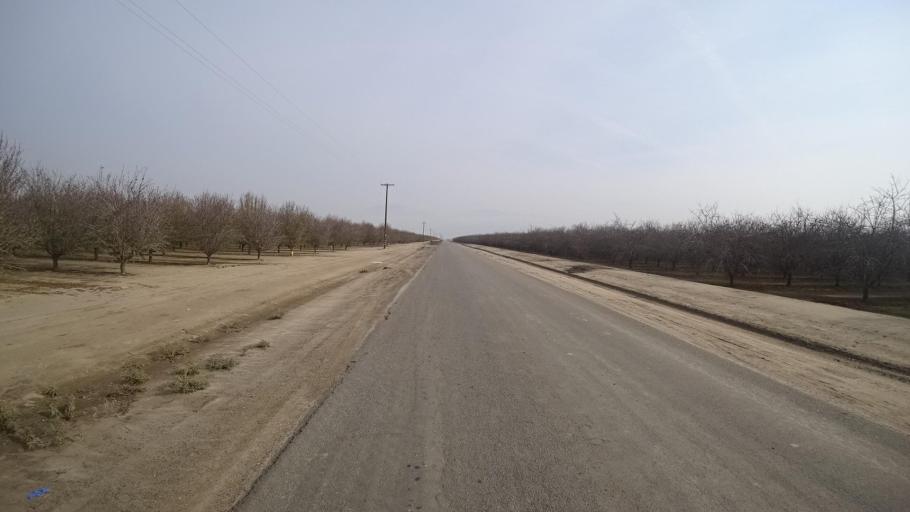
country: US
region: California
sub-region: Kern County
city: Arvin
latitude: 35.1798
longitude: -118.8756
